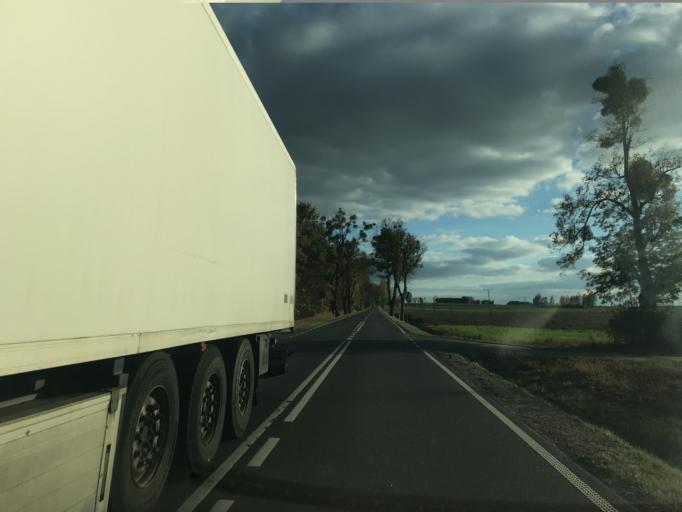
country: PL
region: Warmian-Masurian Voivodeship
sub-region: Powiat dzialdowski
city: Lidzbark
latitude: 53.3628
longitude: 19.8192
